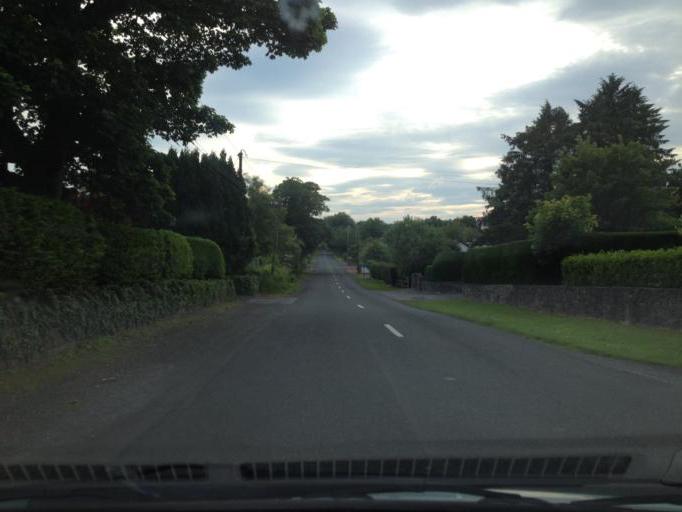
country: IE
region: Connaught
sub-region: Sligo
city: Sligo
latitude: 54.2806
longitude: -8.4324
